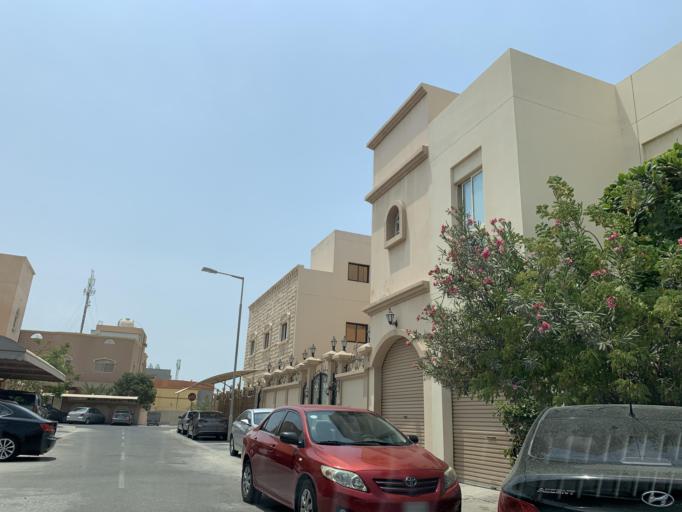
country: BH
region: Muharraq
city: Al Hadd
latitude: 26.2769
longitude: 50.6475
